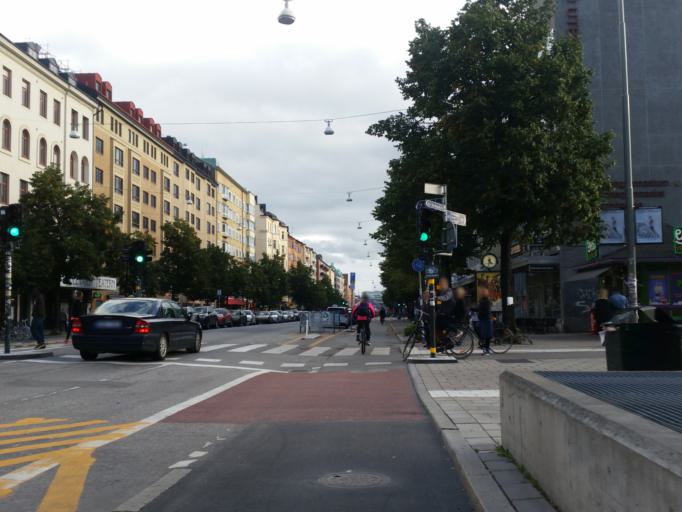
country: SE
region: Stockholm
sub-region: Stockholms Kommun
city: Stockholm
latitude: 59.3118
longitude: 18.0744
